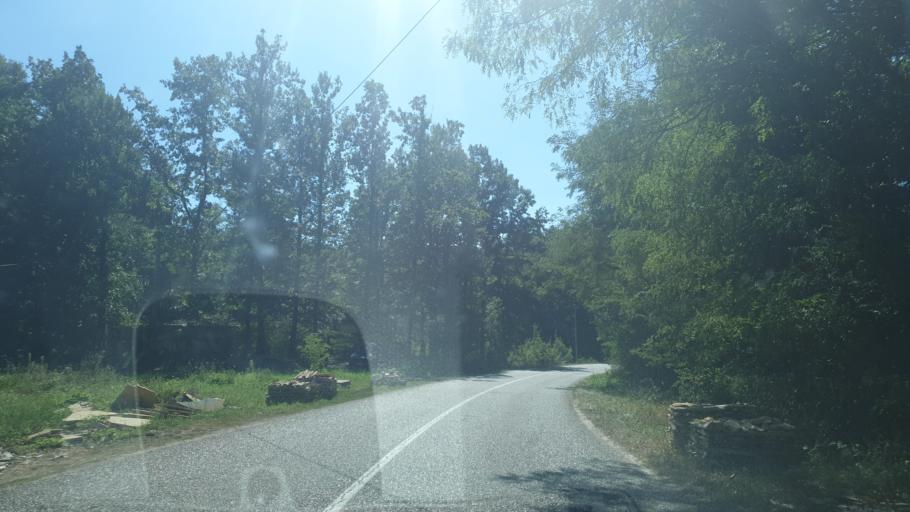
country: RS
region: Central Serbia
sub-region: Kolubarski Okrug
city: Mionica
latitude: 44.2013
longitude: 20.0800
